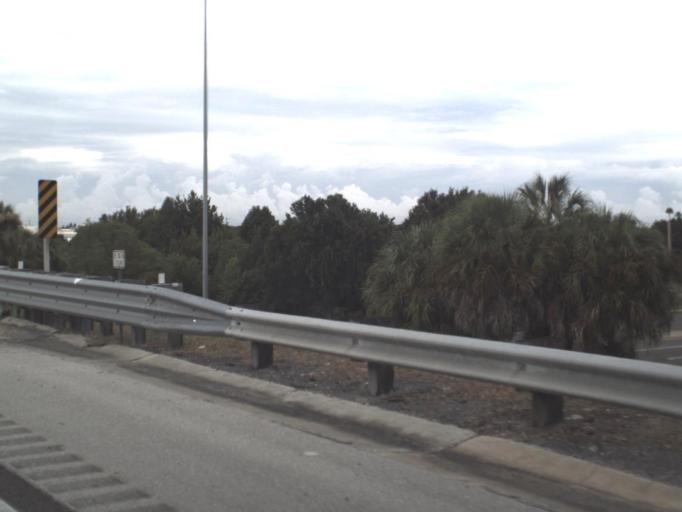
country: US
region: Florida
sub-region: Sarasota County
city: Lake Sarasota
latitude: 27.2993
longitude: -82.4483
